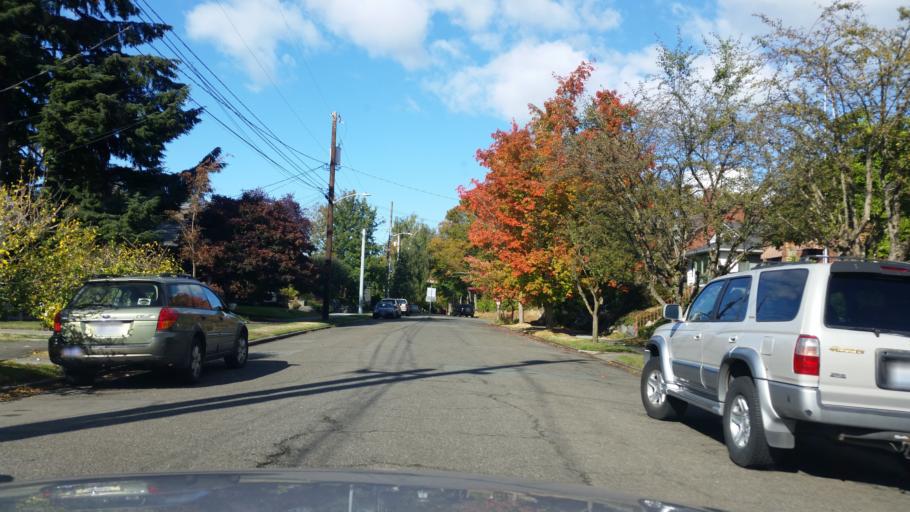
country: US
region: Washington
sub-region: King County
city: Seattle
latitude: 47.6425
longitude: -122.3676
